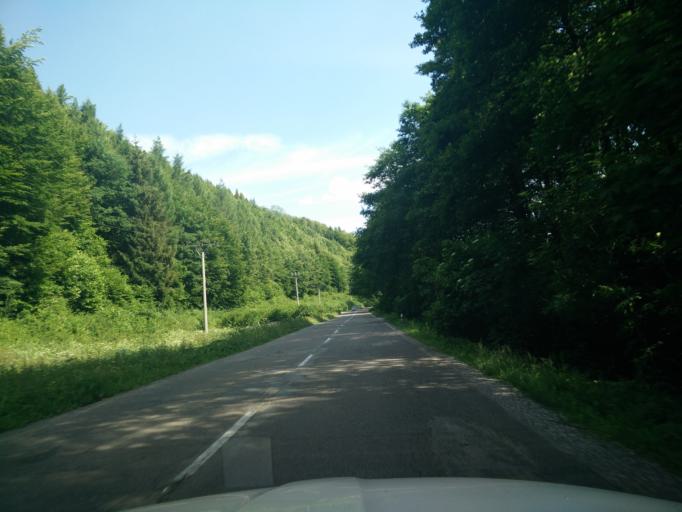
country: SK
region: Nitriansky
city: Bojnice
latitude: 48.9301
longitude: 18.6395
